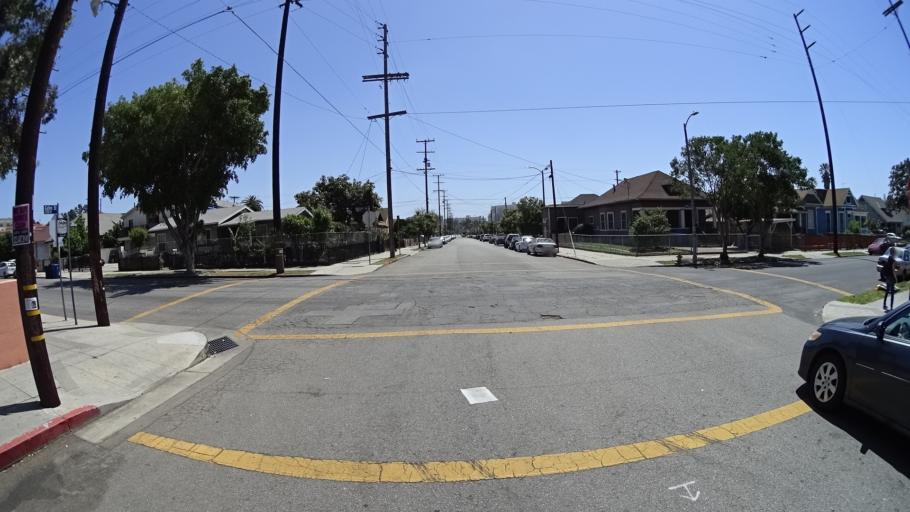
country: US
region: California
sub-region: Los Angeles County
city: Boyle Heights
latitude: 34.0721
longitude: -118.2064
